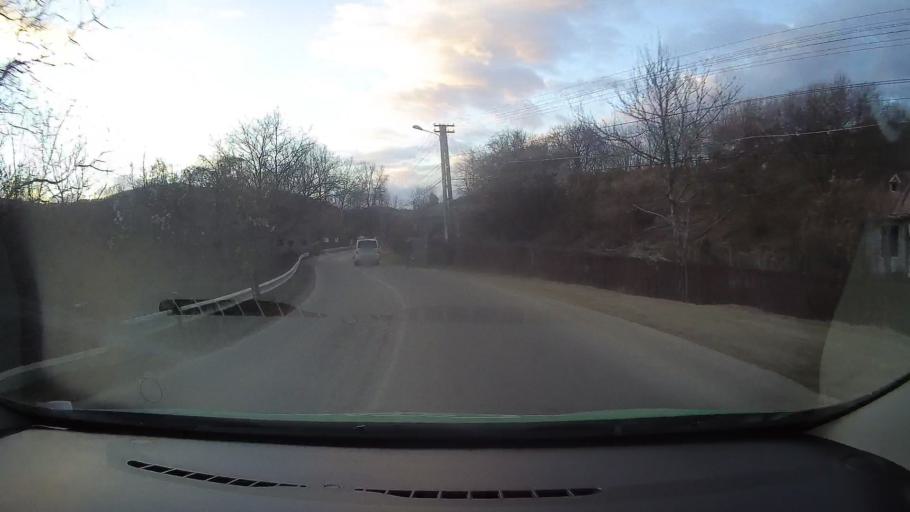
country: RO
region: Dambovita
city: Iedera de Jos
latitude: 45.0180
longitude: 25.6396
